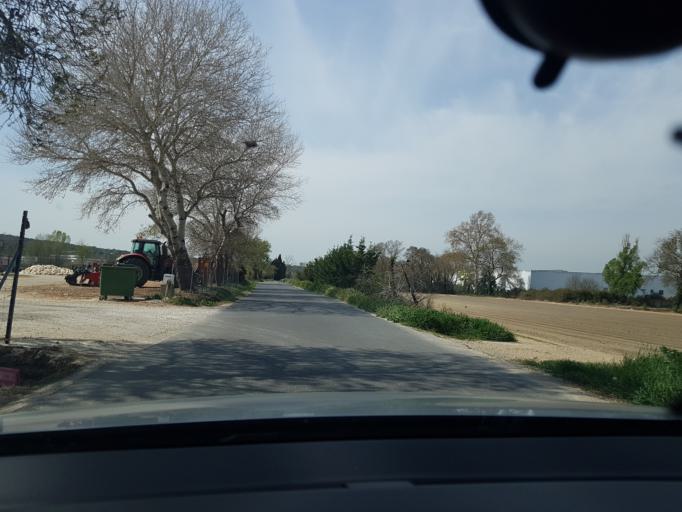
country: FR
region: Provence-Alpes-Cote d'Azur
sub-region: Departement des Bouches-du-Rhone
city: Bouc-Bel-Air
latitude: 43.4763
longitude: 5.3879
